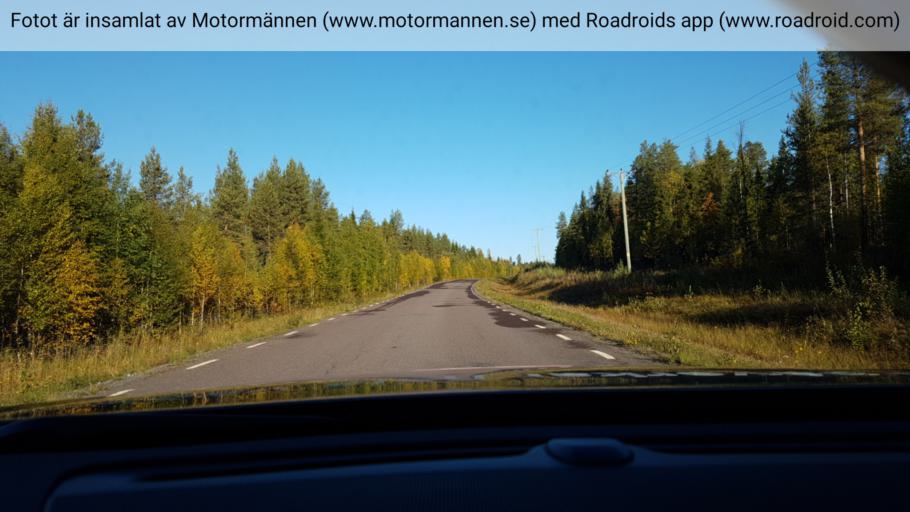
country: SE
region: Norrbotten
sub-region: Bodens Kommun
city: Boden
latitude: 66.0689
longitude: 21.3986
